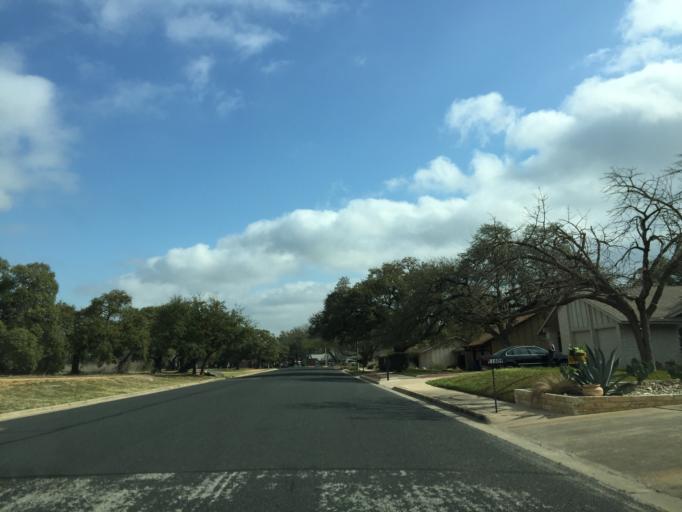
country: US
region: Texas
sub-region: Williamson County
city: Jollyville
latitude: 30.4126
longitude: -97.7369
